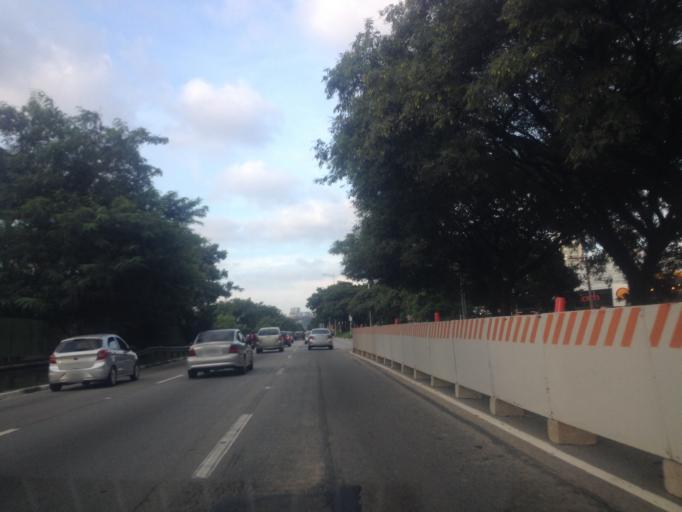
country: BR
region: Sao Paulo
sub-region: Taboao Da Serra
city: Taboao da Serra
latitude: -23.6379
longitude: -46.7225
